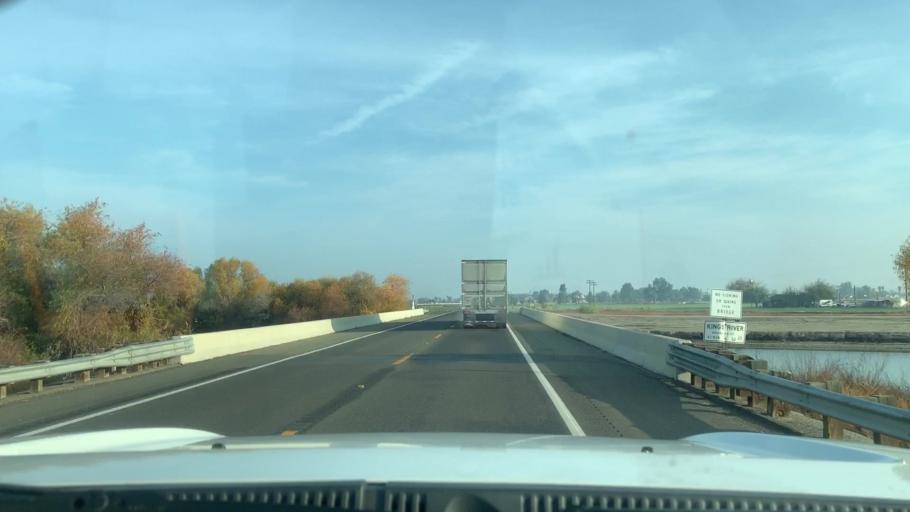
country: US
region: California
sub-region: Kings County
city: Stratford
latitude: 36.1800
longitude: -119.8347
